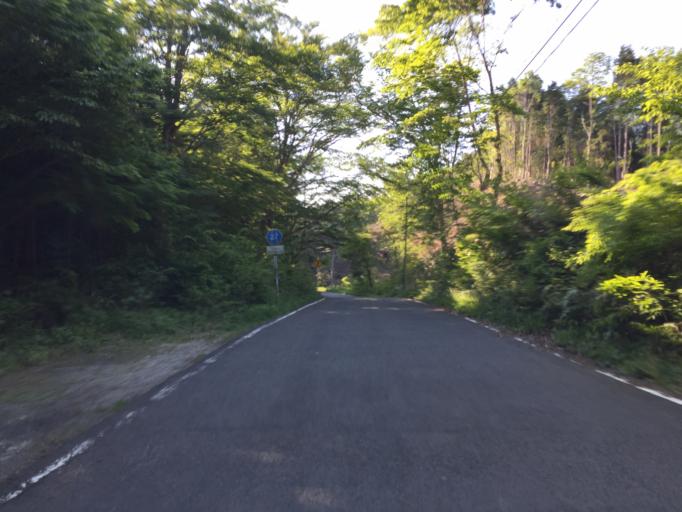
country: JP
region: Ibaraki
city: Kitaibaraki
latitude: 36.8958
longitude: 140.5994
